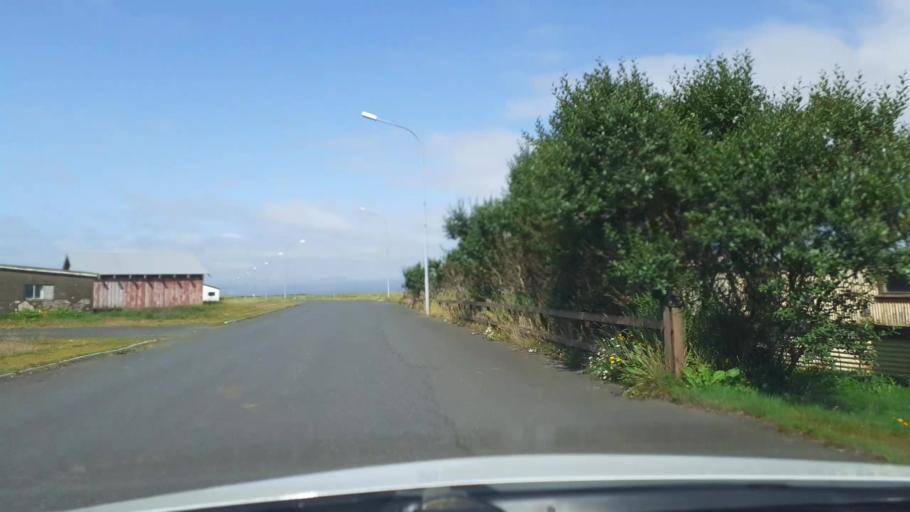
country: IS
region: South
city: Hveragerdi
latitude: 63.8661
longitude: -21.1558
